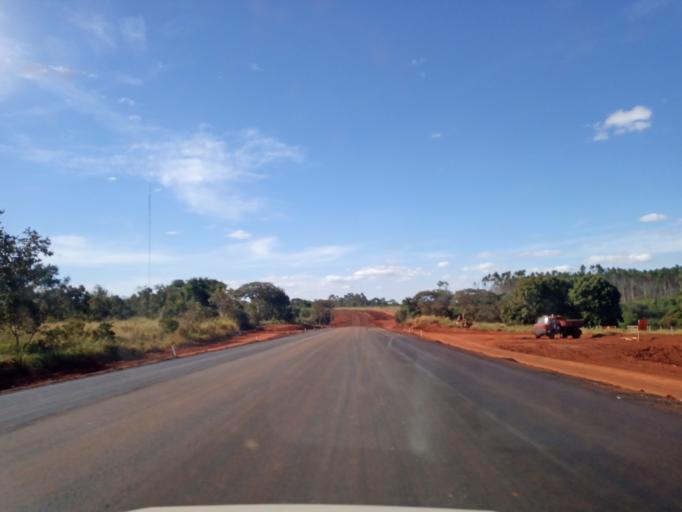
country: BR
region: Minas Gerais
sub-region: Ituiutaba
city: Ituiutaba
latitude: -18.9804
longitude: -49.5082
